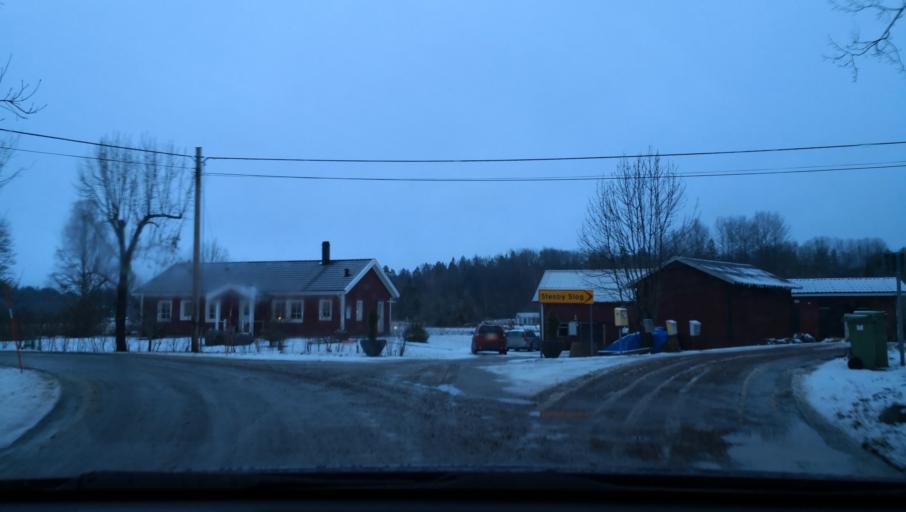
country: SE
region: Vaestmanland
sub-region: Kungsors Kommun
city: Kungsoer
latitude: 59.4018
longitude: 16.2037
